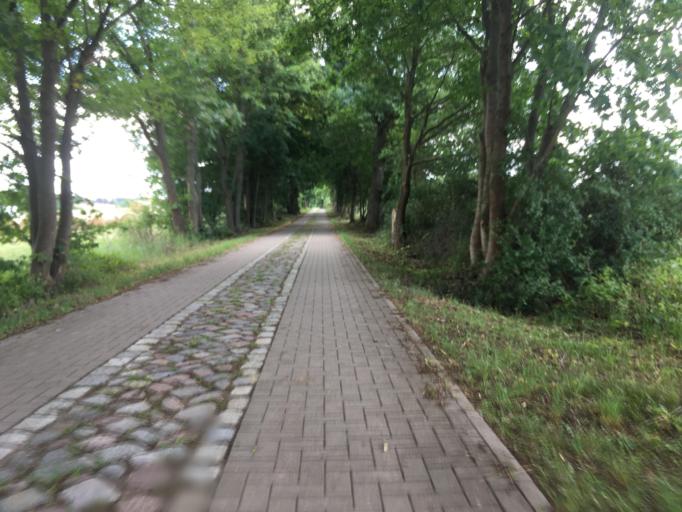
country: DE
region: Brandenburg
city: Althuttendorf
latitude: 52.9794
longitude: 13.8206
